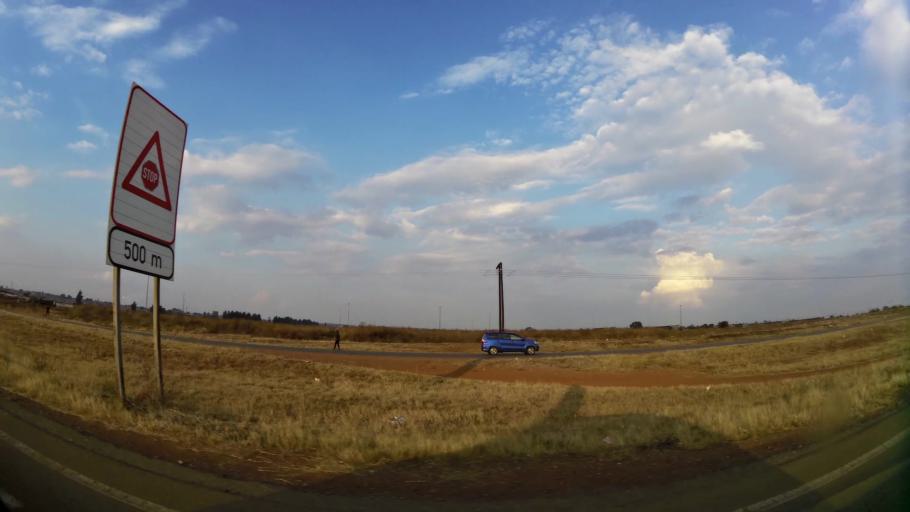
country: ZA
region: Gauteng
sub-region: Sedibeng District Municipality
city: Vanderbijlpark
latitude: -26.5948
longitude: 27.8203
